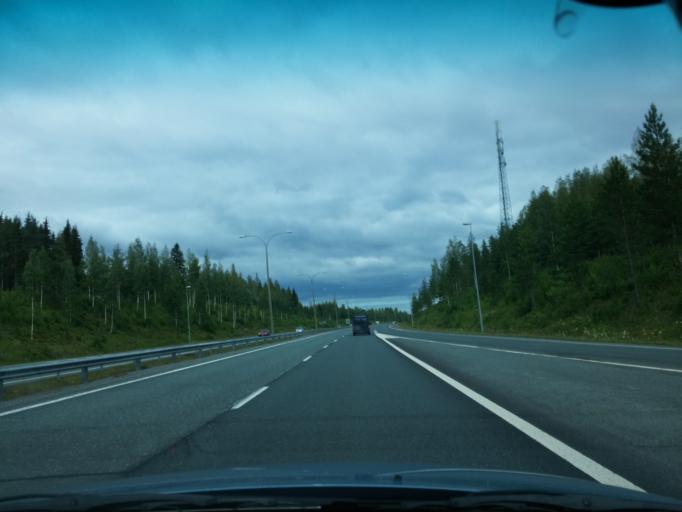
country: FI
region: Northern Savo
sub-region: Kuopio
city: Kuopio
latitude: 62.8020
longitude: 27.5967
